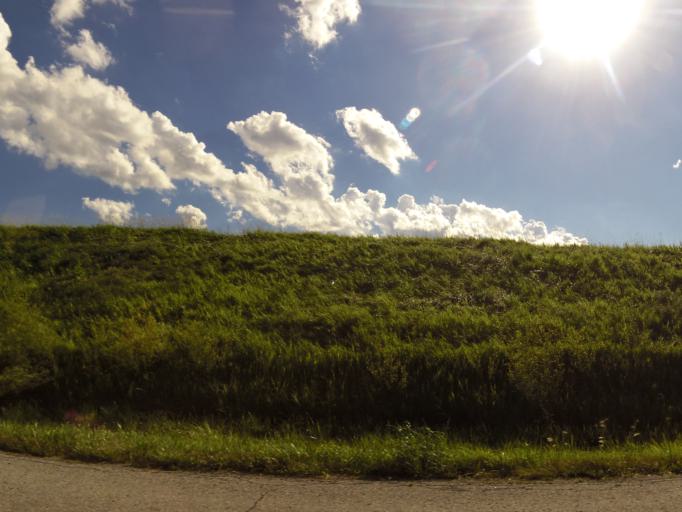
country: US
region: Missouri
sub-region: Marion County
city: Palmyra
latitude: 39.8401
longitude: -91.5224
